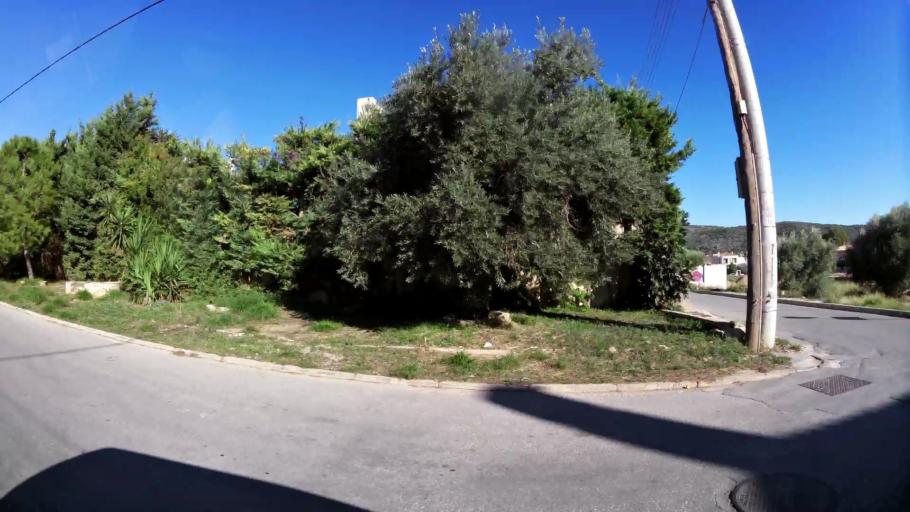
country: GR
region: Attica
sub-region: Nomarchia Anatolikis Attikis
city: Vari
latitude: 37.8355
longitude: 23.8139
